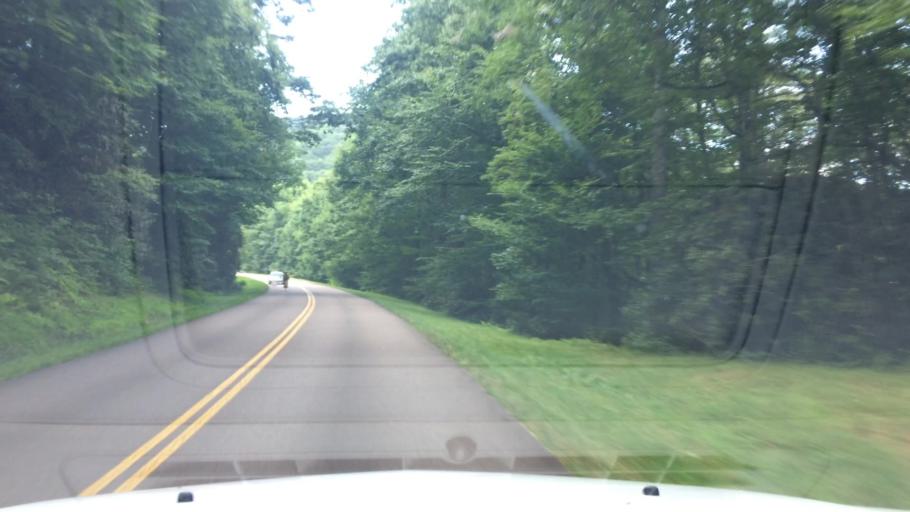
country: US
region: North Carolina
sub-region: Watauga County
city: Blowing Rock
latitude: 36.1553
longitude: -81.6687
